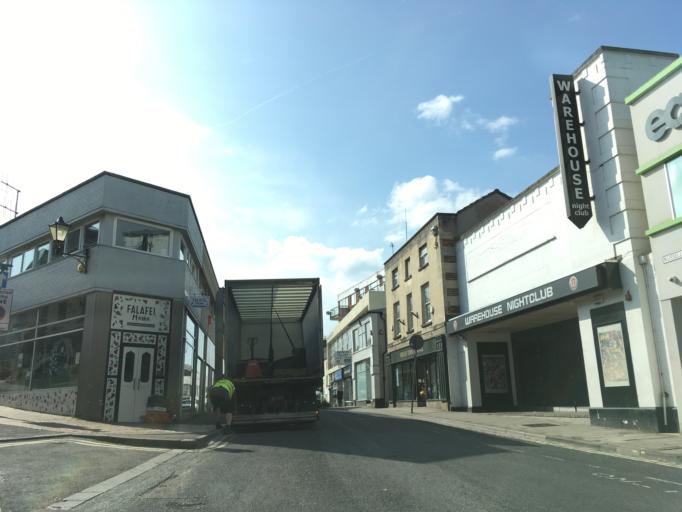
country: GB
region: England
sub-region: Gloucestershire
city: Stroud
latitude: 51.7445
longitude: -2.2172
